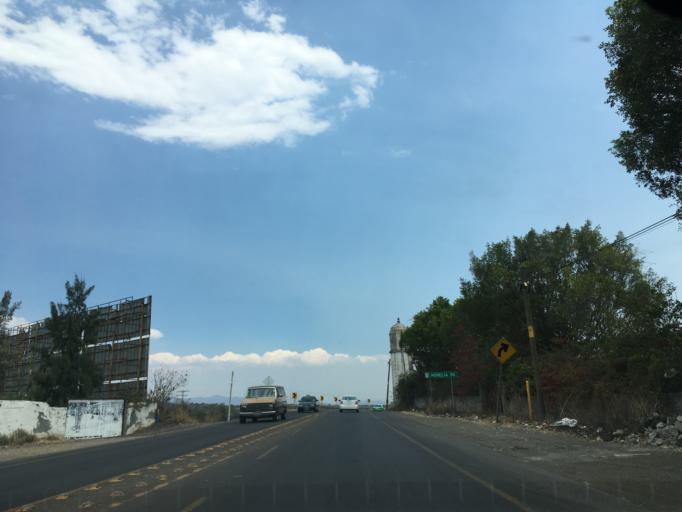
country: MX
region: Guanajuato
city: Moroleon
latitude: 20.1007
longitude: -101.1614
